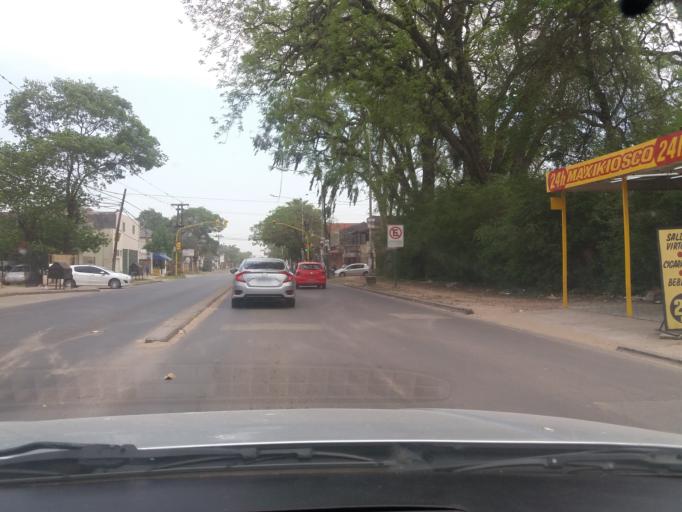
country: AR
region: Corrientes
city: Corrientes
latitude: -27.4947
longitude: -58.8176
